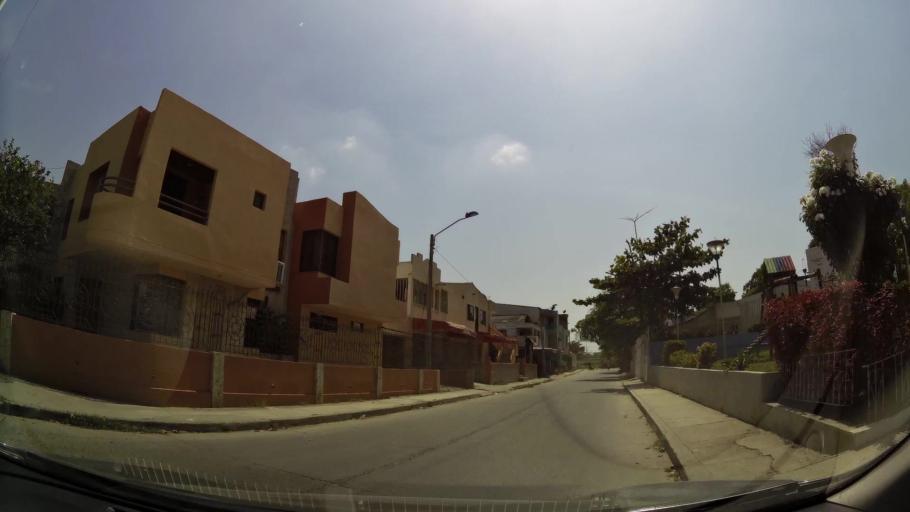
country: CO
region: Bolivar
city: Cartagena
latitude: 10.4008
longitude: -75.4918
